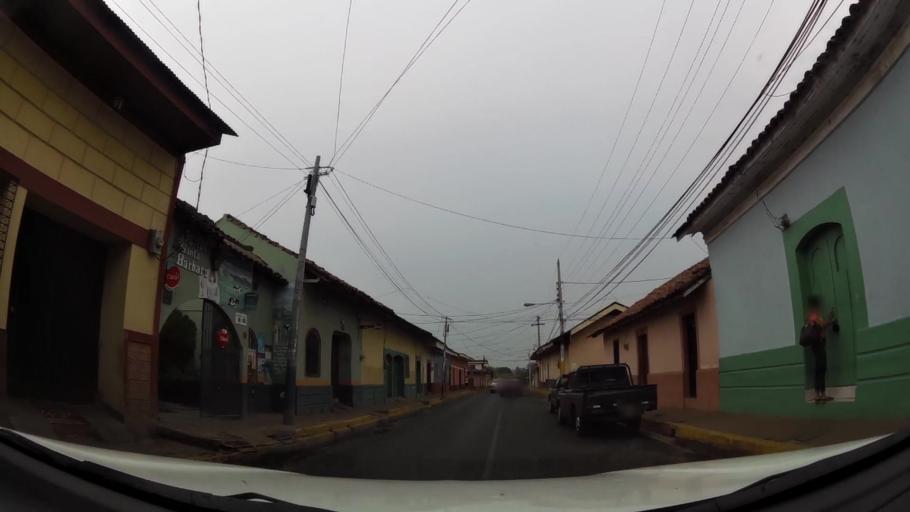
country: NI
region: Leon
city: Leon
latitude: 12.4326
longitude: -86.8803
